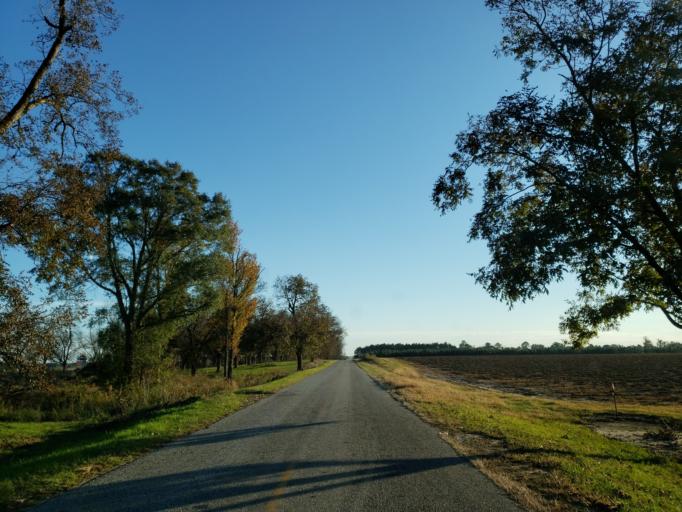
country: US
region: Georgia
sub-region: Dooly County
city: Vienna
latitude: 32.1571
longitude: -83.7605
